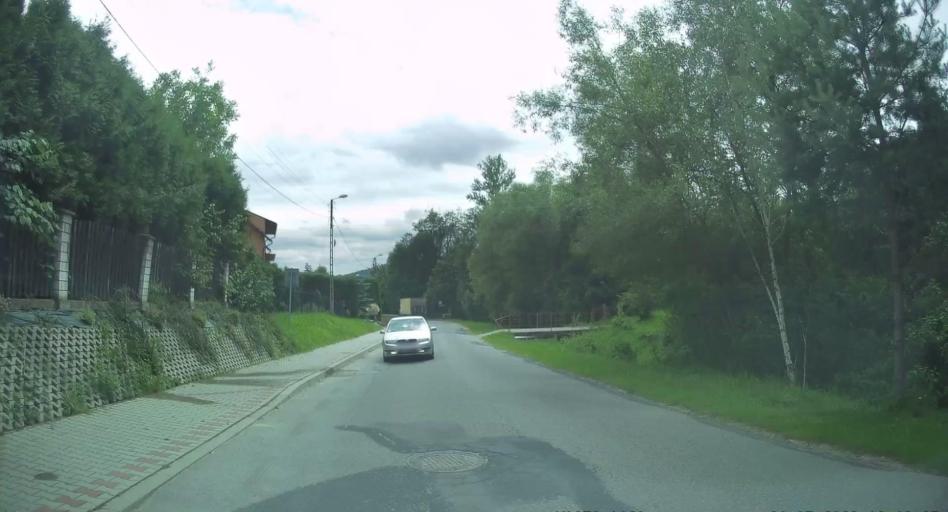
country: PL
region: Lesser Poland Voivodeship
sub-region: Powiat nowosadecki
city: Muszyna
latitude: 49.3714
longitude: 20.8886
